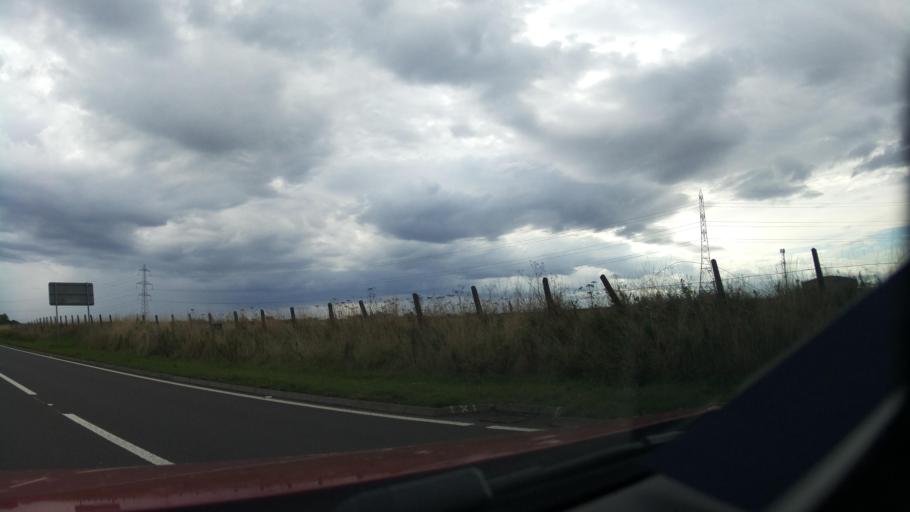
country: GB
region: Scotland
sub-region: Fife
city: High Valleyfield
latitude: 56.0662
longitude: -3.6327
